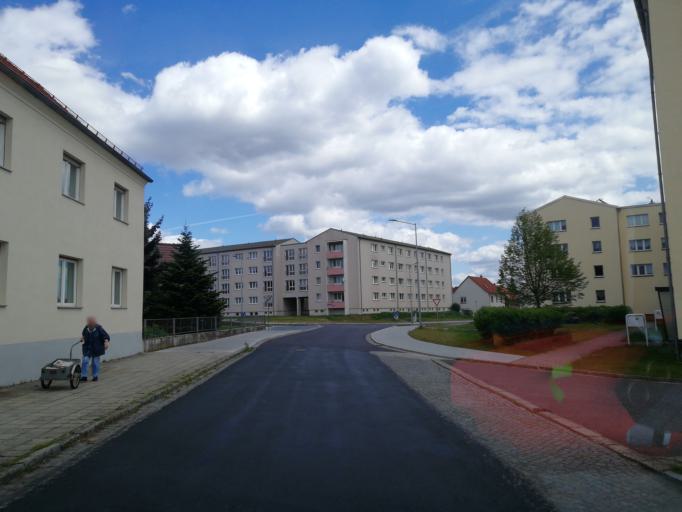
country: DE
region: Brandenburg
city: Lauchhammer
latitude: 51.4966
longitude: 13.7664
